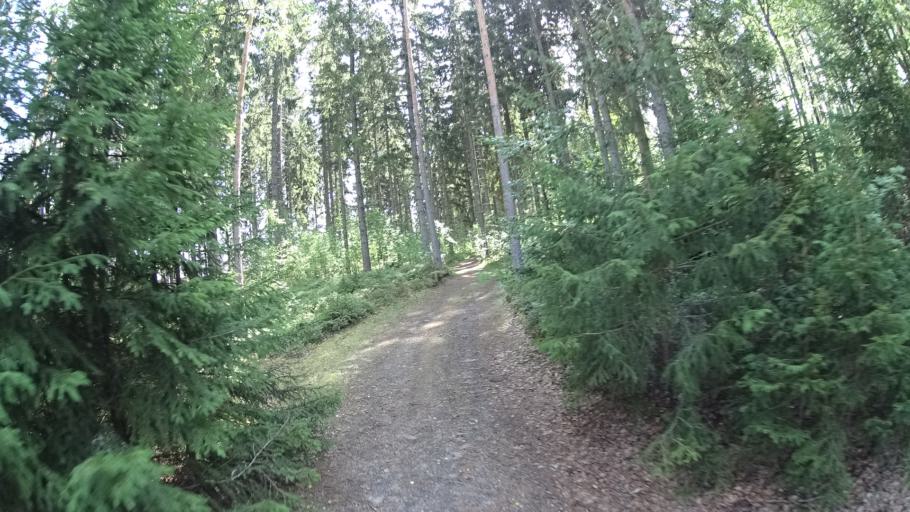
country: FI
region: Haeme
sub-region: Forssa
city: Tammela
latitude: 60.7729
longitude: 23.8676
